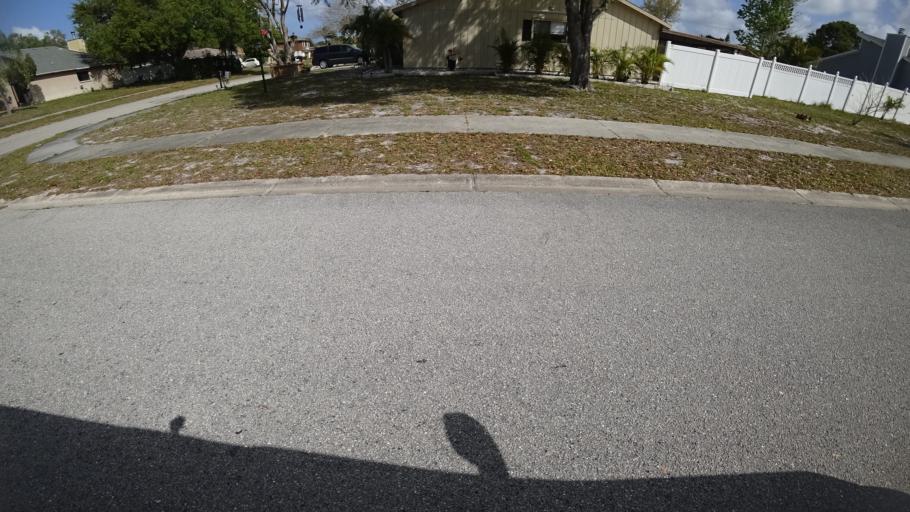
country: US
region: Florida
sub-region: Manatee County
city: Whitfield
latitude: 27.4098
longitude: -82.5628
